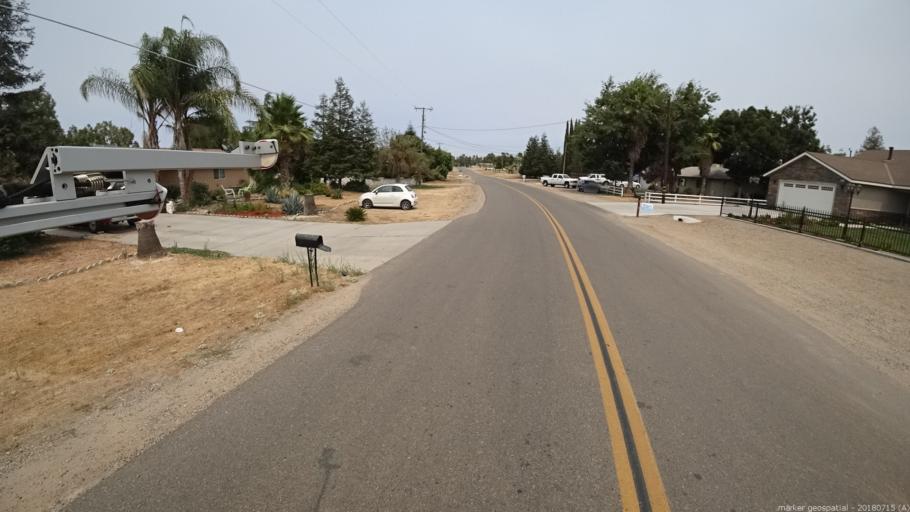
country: US
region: California
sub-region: Madera County
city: Madera Acres
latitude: 37.0026
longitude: -120.0969
